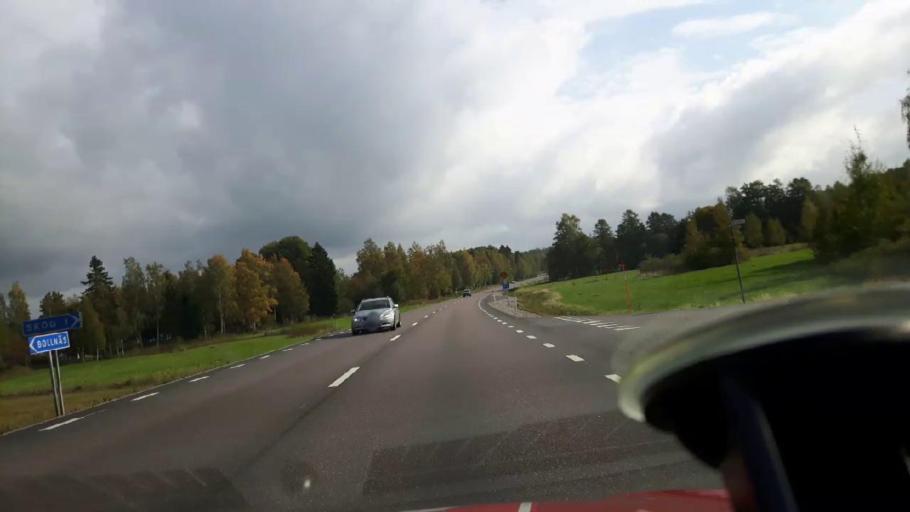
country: SE
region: Gaevleborg
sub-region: Bollnas Kommun
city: Kilafors
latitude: 61.1712
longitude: 16.8118
